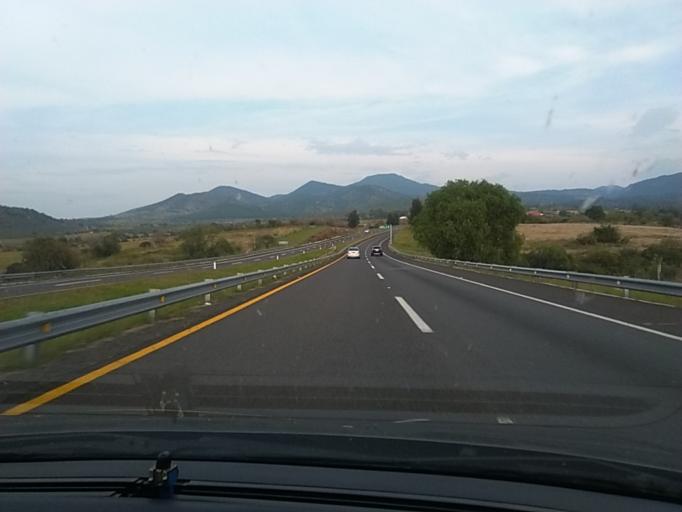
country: MX
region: Michoacan
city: Zinapecuaro
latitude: 19.9027
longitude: -100.8026
